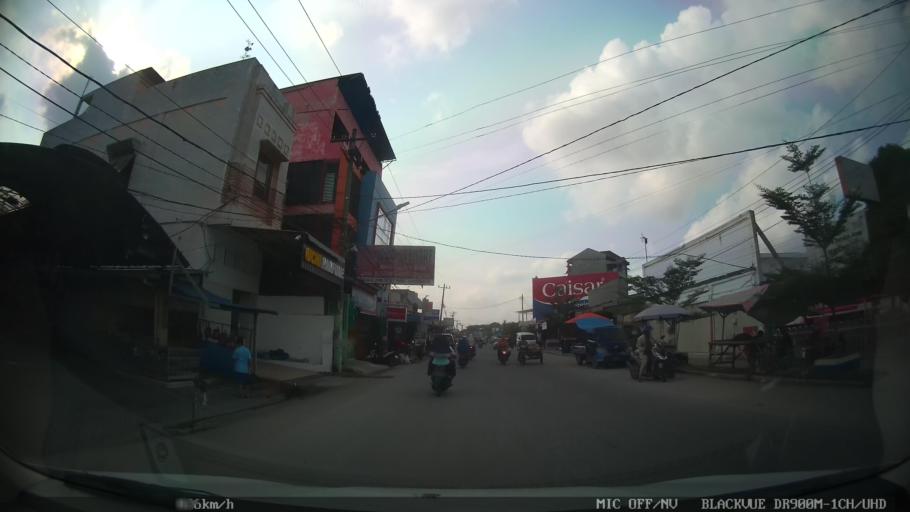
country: ID
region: North Sumatra
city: Medan
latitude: 3.5946
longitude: 98.7540
